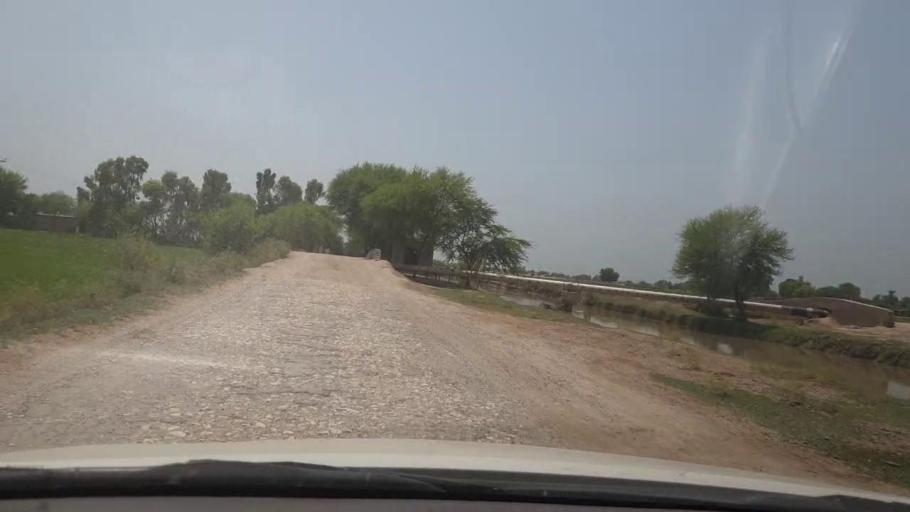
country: PK
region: Sindh
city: Shikarpur
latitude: 28.0945
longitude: 68.5772
